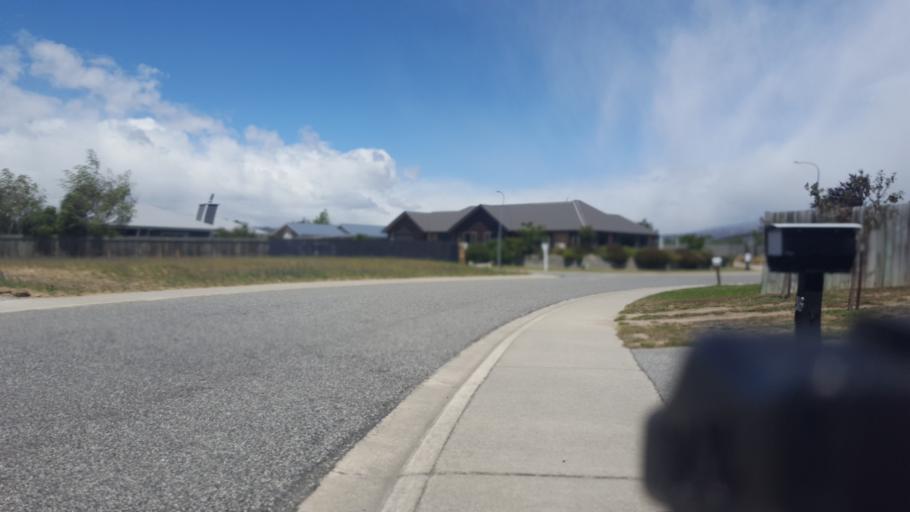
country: NZ
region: Otago
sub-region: Queenstown-Lakes District
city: Wanaka
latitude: -45.1947
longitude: 169.3334
